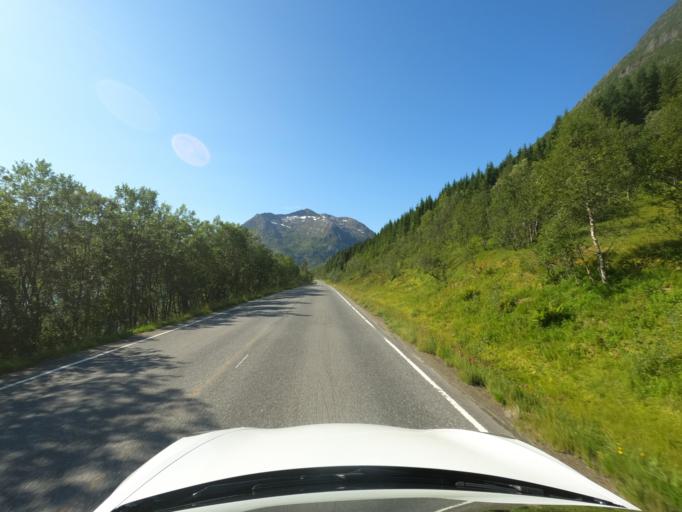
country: NO
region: Nordland
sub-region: Lodingen
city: Lodingen
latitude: 68.5521
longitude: 15.7505
